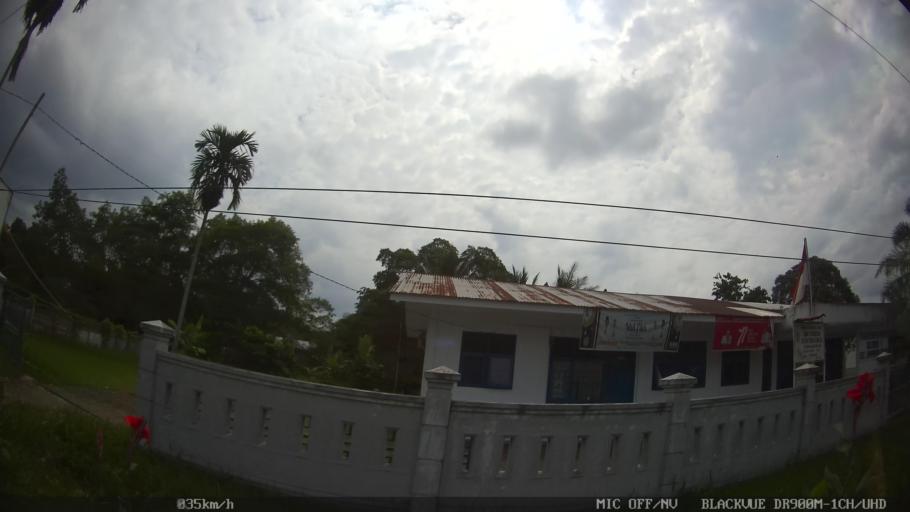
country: ID
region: North Sumatra
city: Sunggal
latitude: 3.6340
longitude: 98.5934
